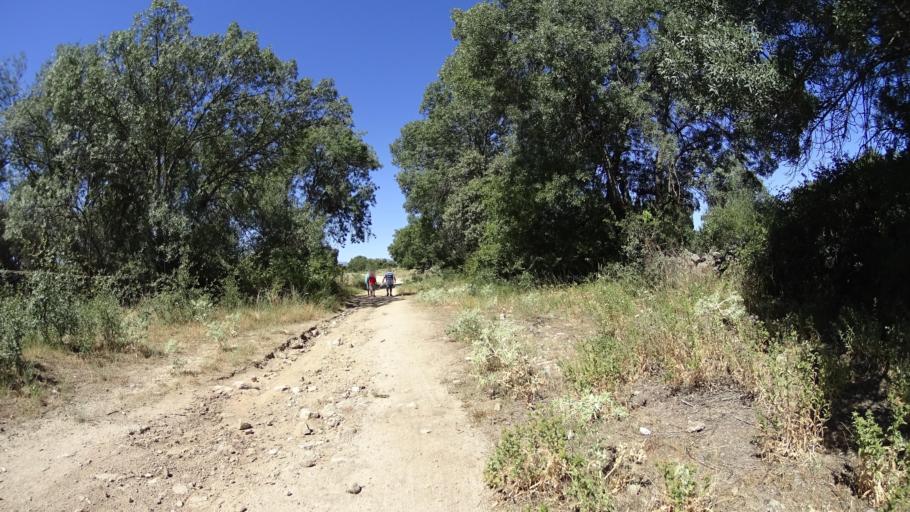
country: ES
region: Madrid
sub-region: Provincia de Madrid
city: Collado-Villalba
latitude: 40.6492
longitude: -4.0118
